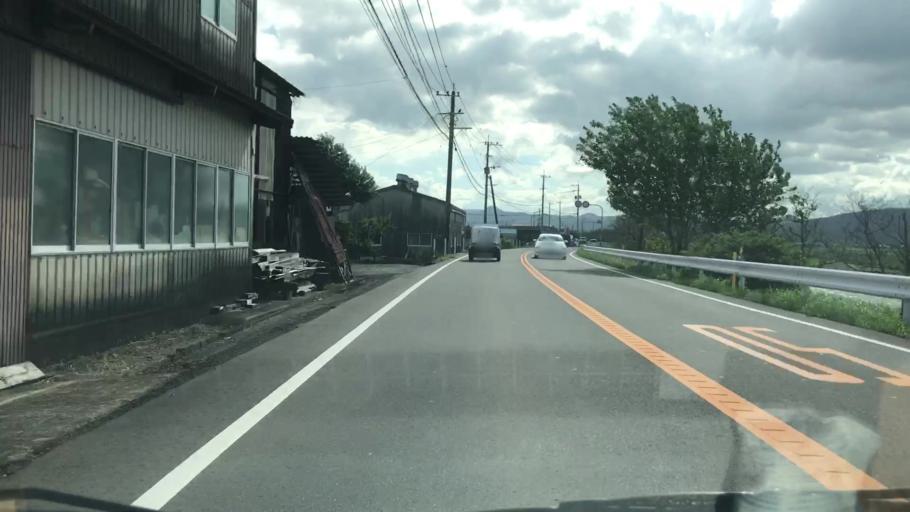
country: JP
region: Saga Prefecture
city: Kashima
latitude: 33.1559
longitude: 130.1591
